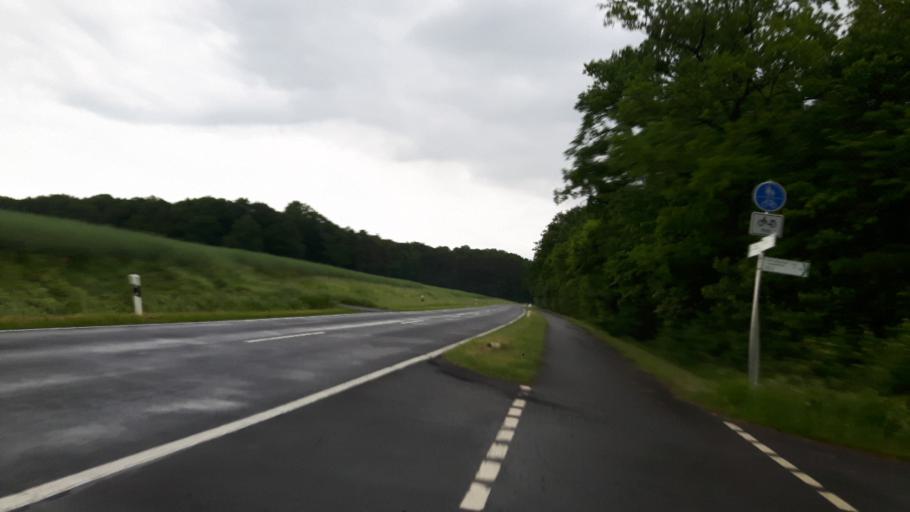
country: DE
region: Bavaria
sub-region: Regierungsbezirk Unterfranken
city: Uchtelhausen
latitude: 50.1265
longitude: 10.2898
